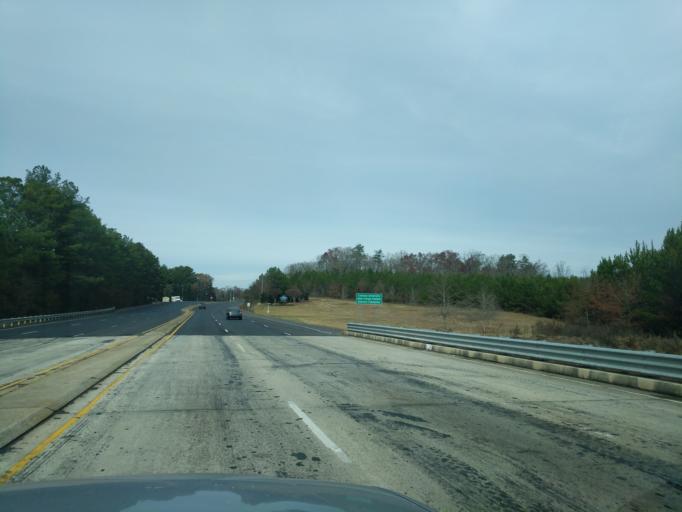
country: US
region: South Carolina
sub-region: Anderson County
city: Pendleton
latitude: 34.6522
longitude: -82.8098
